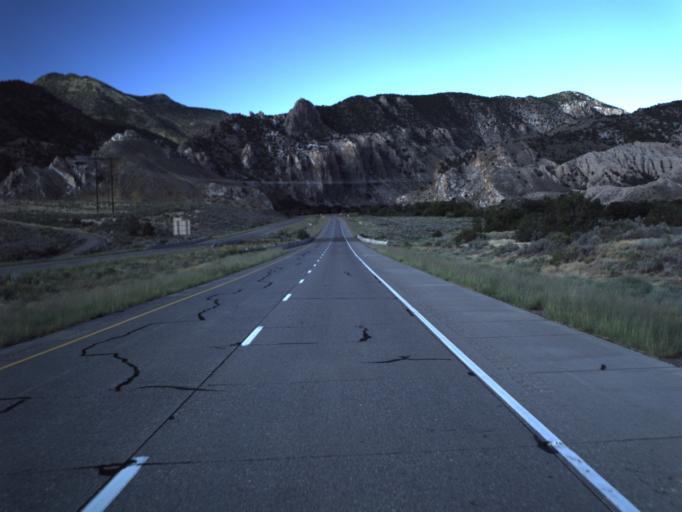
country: US
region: Utah
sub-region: Sevier County
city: Monroe
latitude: 38.5890
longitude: -112.2714
